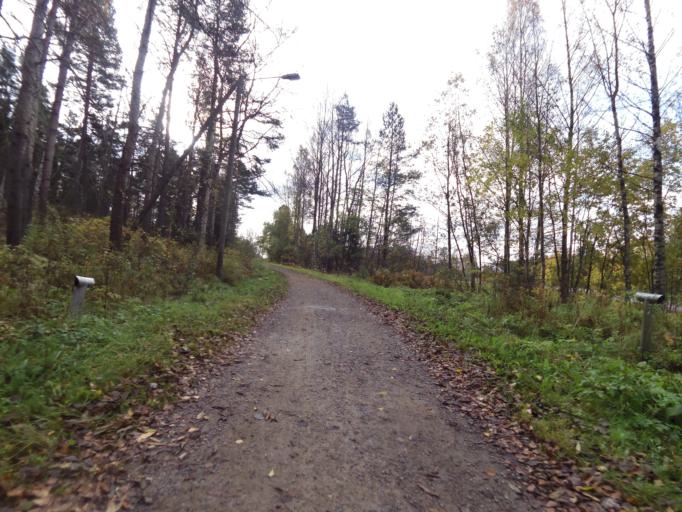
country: FI
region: Uusimaa
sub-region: Helsinki
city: Kauniainen
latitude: 60.1753
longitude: 24.6987
